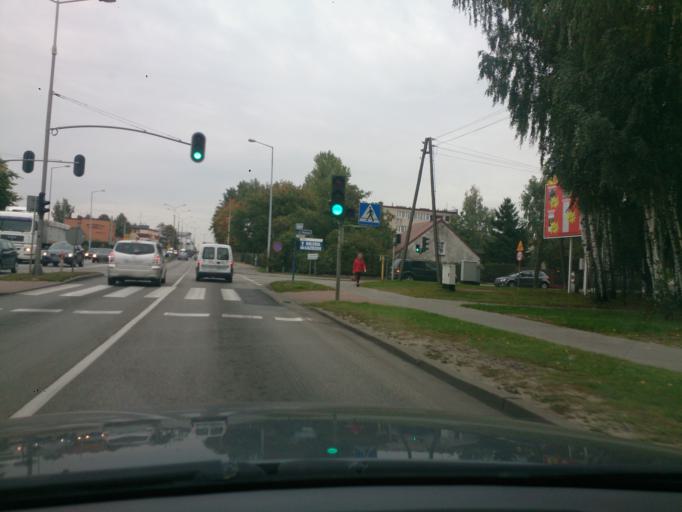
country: PL
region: Pomeranian Voivodeship
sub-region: Powiat wejherowski
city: Rumia
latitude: 54.5625
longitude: 18.3955
